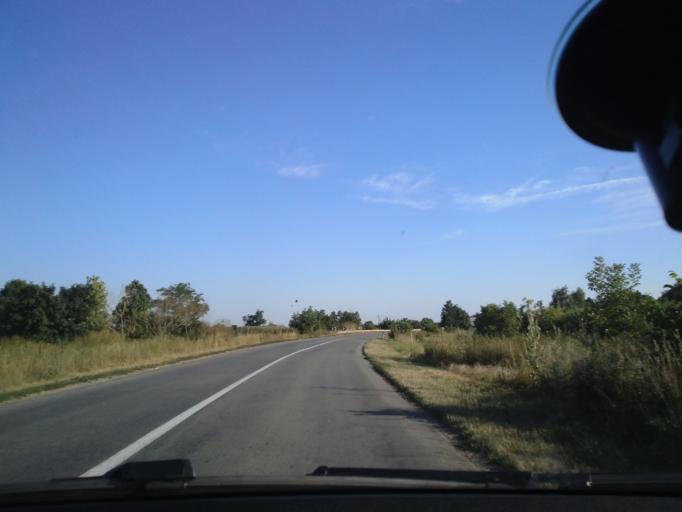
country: RS
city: Doroslovo
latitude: 45.6172
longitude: 19.1968
